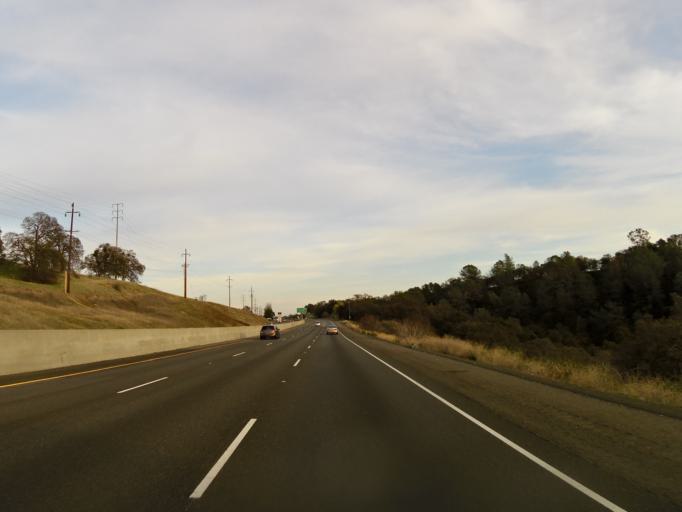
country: US
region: California
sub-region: El Dorado County
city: Cameron Park
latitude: 38.6550
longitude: -121.0193
